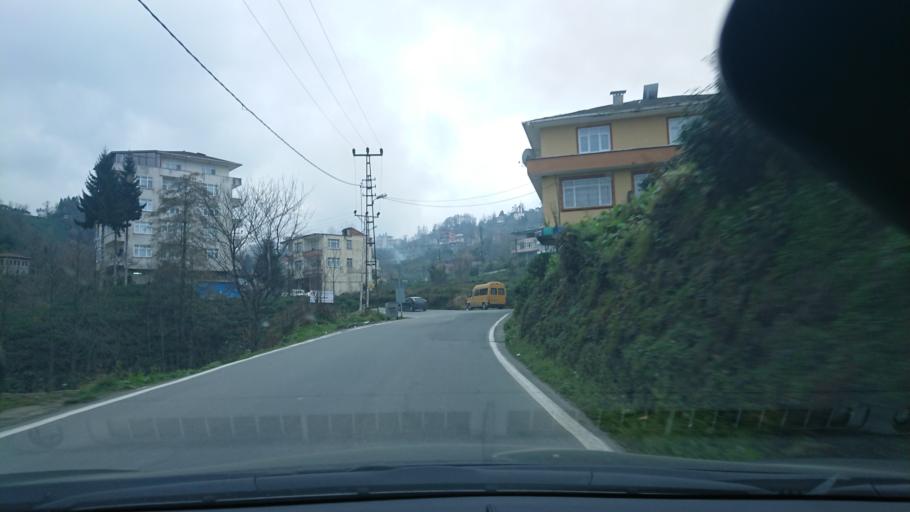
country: TR
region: Rize
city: Rize
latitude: 41.0253
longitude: 40.5039
